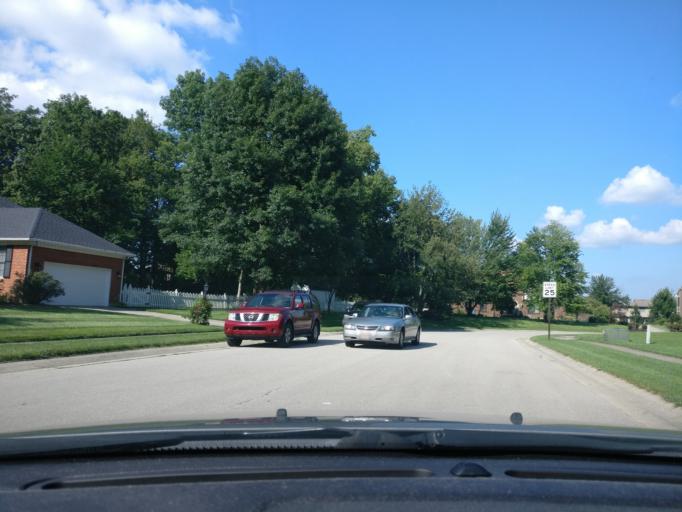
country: US
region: Ohio
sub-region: Warren County
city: Springboro
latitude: 39.5735
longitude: -84.2469
